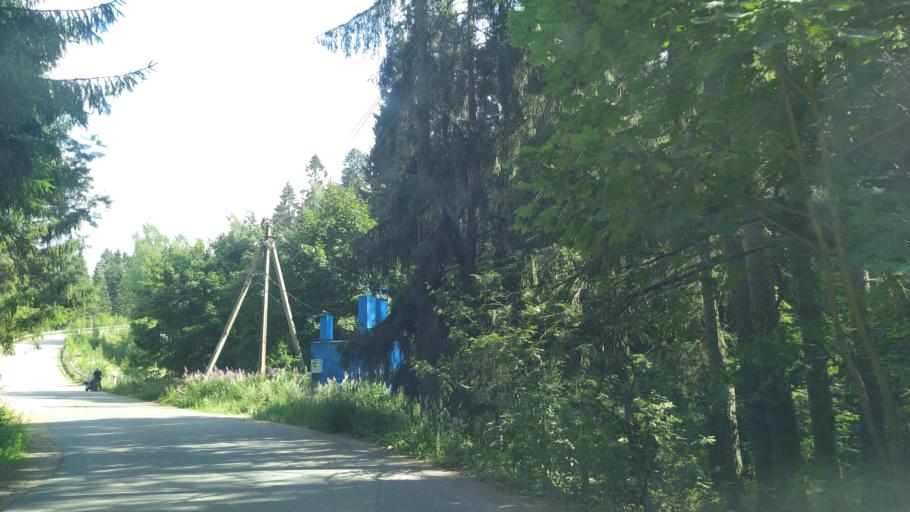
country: RU
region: Leningrad
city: Toksovo
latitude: 60.1681
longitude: 30.5330
